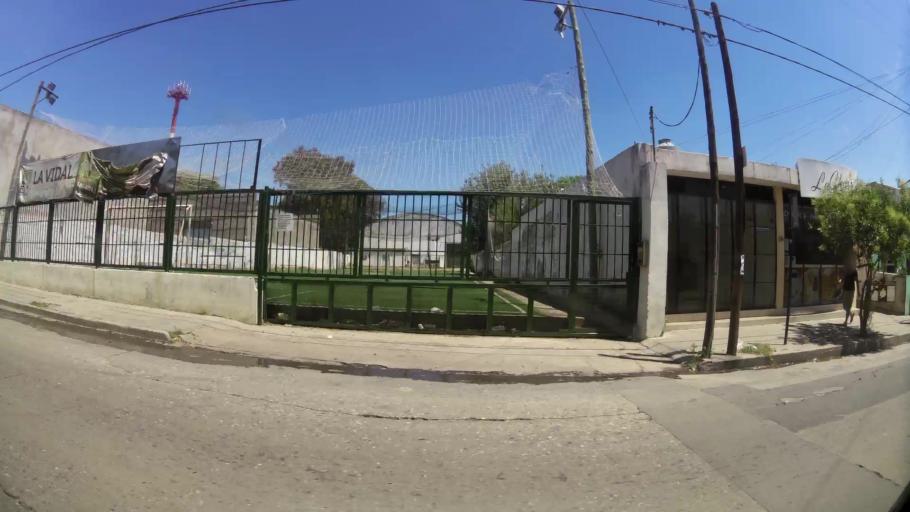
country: AR
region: Cordoba
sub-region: Departamento de Capital
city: Cordoba
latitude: -31.4121
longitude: -64.2254
